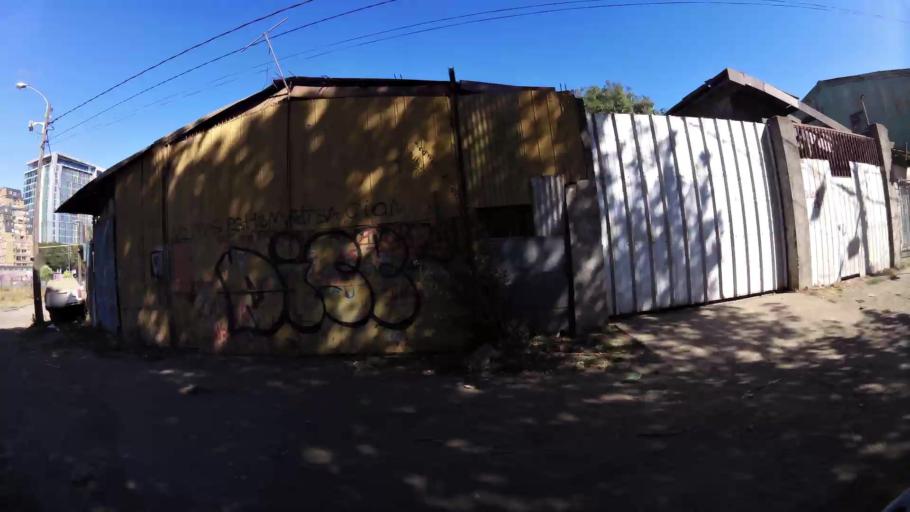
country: CL
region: Biobio
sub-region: Provincia de Concepcion
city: Concepcion
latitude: -36.8330
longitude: -73.0596
